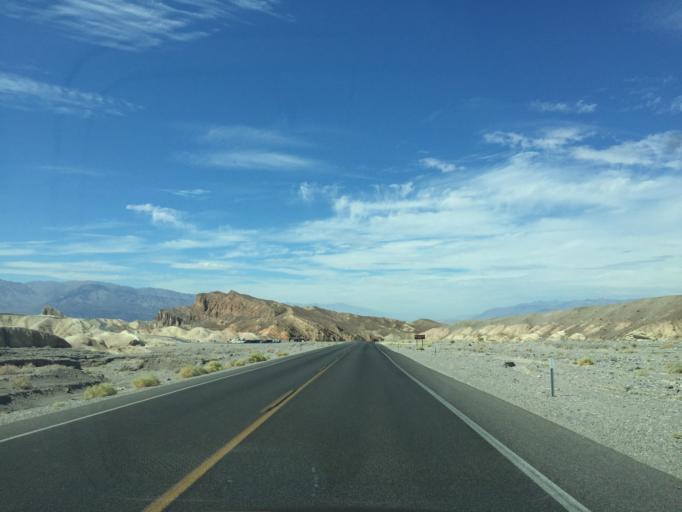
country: US
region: Nevada
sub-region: Nye County
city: Beatty
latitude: 36.4191
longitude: -116.8065
